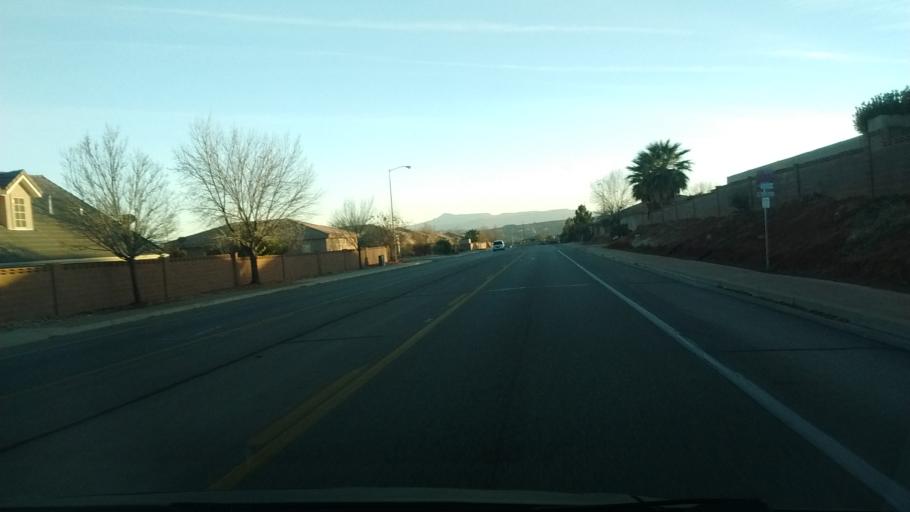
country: US
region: Utah
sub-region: Washington County
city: Washington
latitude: 37.1085
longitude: -113.5318
